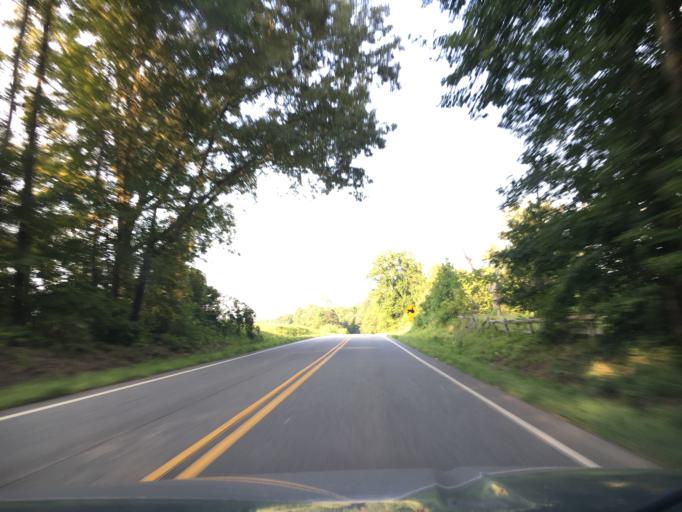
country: US
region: Virginia
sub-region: Halifax County
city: Mountain Road
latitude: 36.8318
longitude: -79.0729
